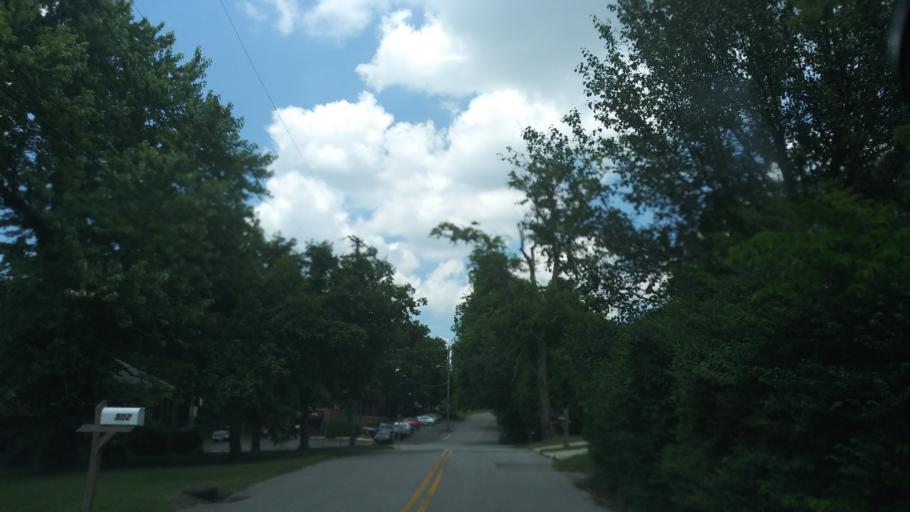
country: US
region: Tennessee
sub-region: Davidson County
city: Nashville
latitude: 36.1421
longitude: -86.8258
